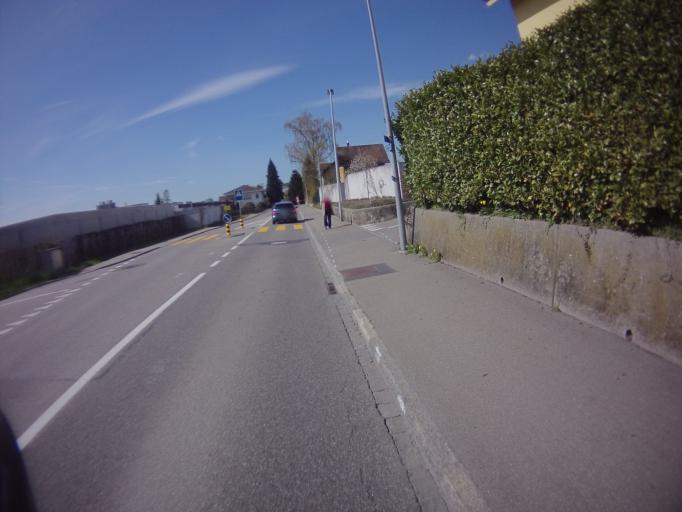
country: CH
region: Aargau
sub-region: Bezirk Baden
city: Niederrohrdorf
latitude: 47.4219
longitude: 8.3135
